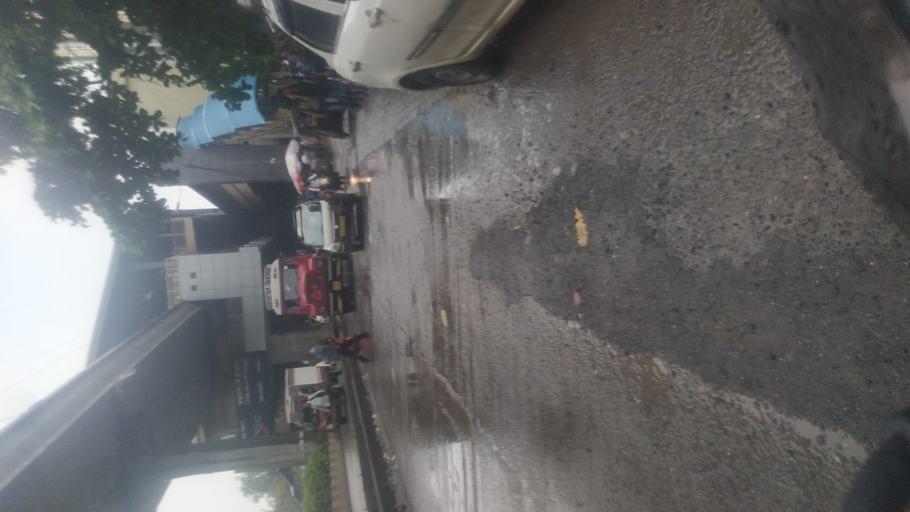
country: IN
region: Maharashtra
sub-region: Mumbai Suburban
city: Powai
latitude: 19.1118
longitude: 72.8689
